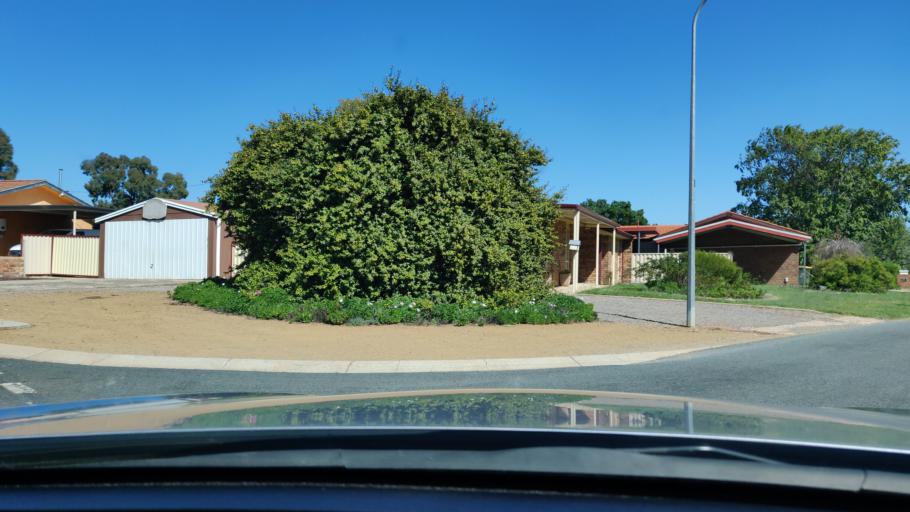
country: AU
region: Australian Capital Territory
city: Macarthur
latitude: -35.4390
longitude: 149.0963
